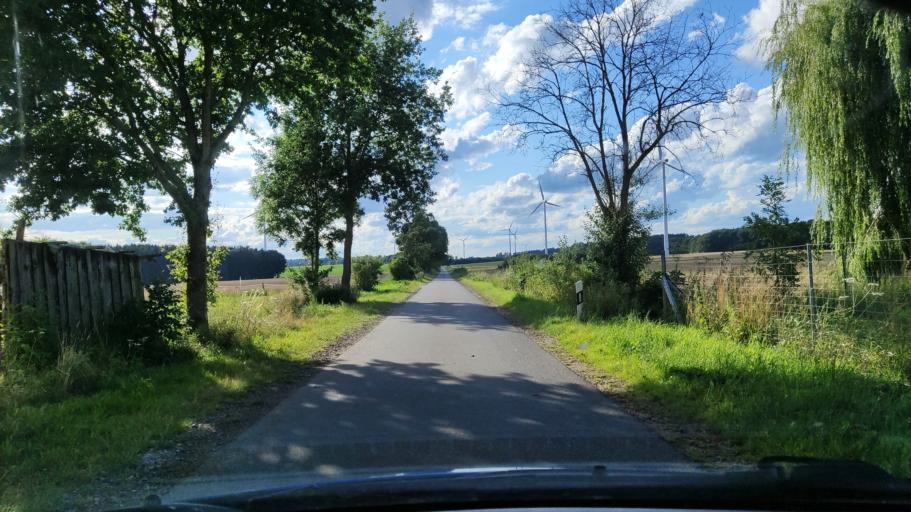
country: DE
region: Lower Saxony
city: Nahrendorf
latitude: 53.1743
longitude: 10.8097
